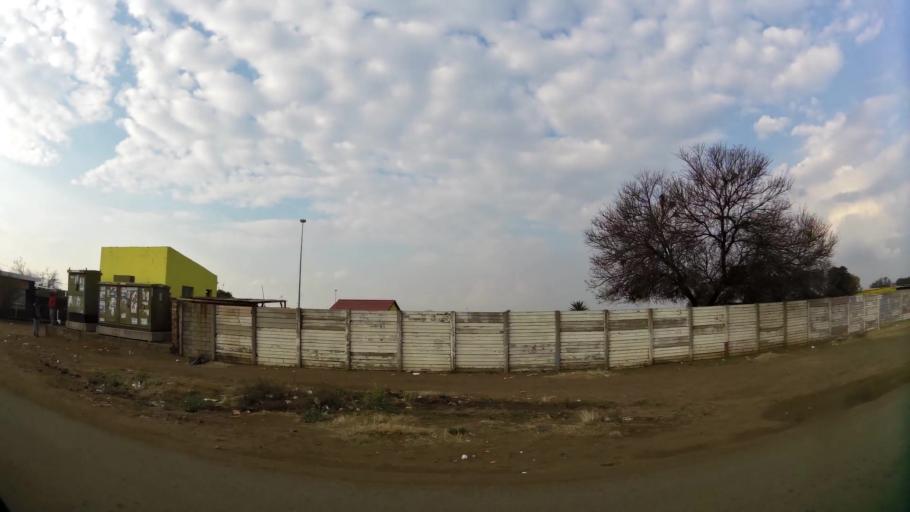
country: ZA
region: Gauteng
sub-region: Sedibeng District Municipality
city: Vanderbijlpark
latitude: -26.6806
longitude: 27.8763
